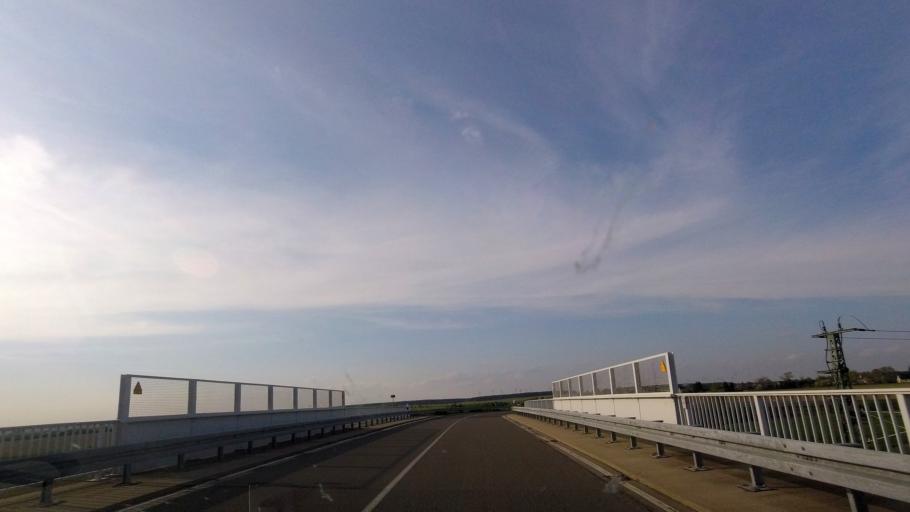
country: DE
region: Saxony-Anhalt
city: Zahna
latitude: 51.9413
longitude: 12.8357
